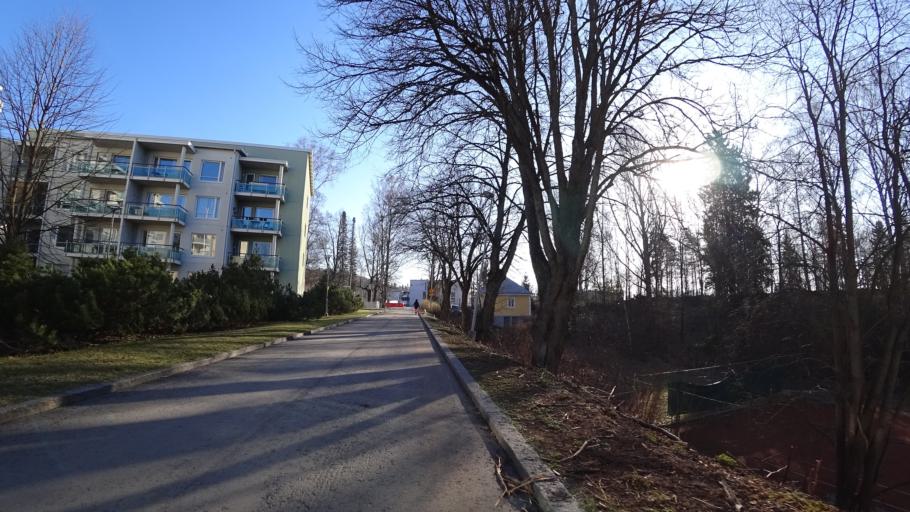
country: FI
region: Pirkanmaa
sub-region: Tampere
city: Pirkkala
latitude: 61.5063
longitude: 23.6611
